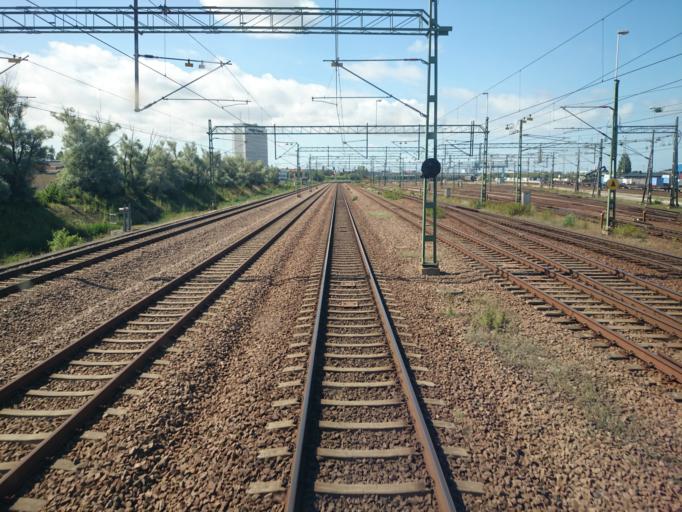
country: SE
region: Skane
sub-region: Burlovs Kommun
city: Arloev
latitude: 55.6216
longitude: 13.0507
